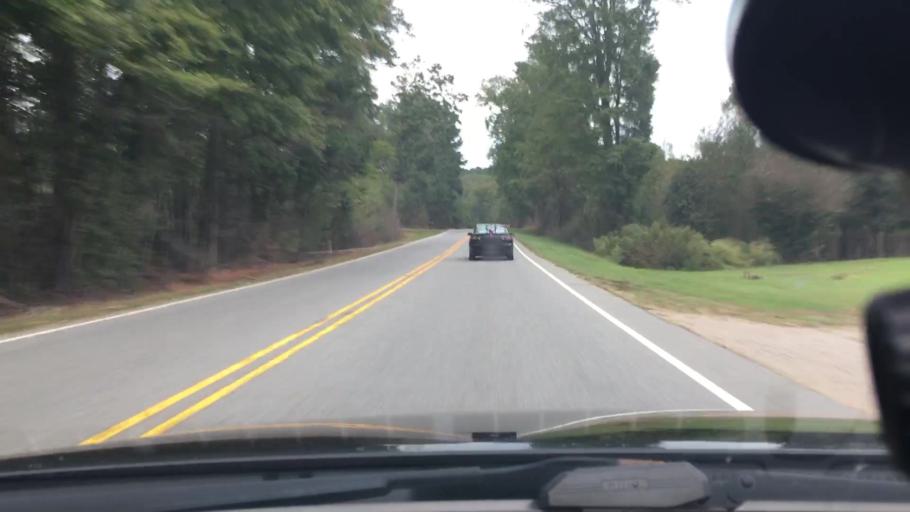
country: US
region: North Carolina
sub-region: Moore County
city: Robbins
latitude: 35.3897
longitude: -79.6453
